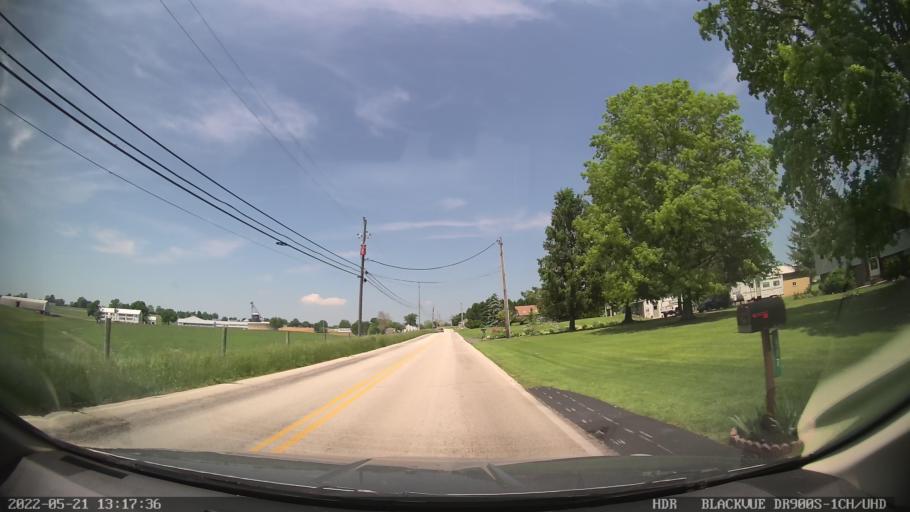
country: US
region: Pennsylvania
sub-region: Berks County
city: Bally
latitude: 40.3604
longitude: -75.5915
